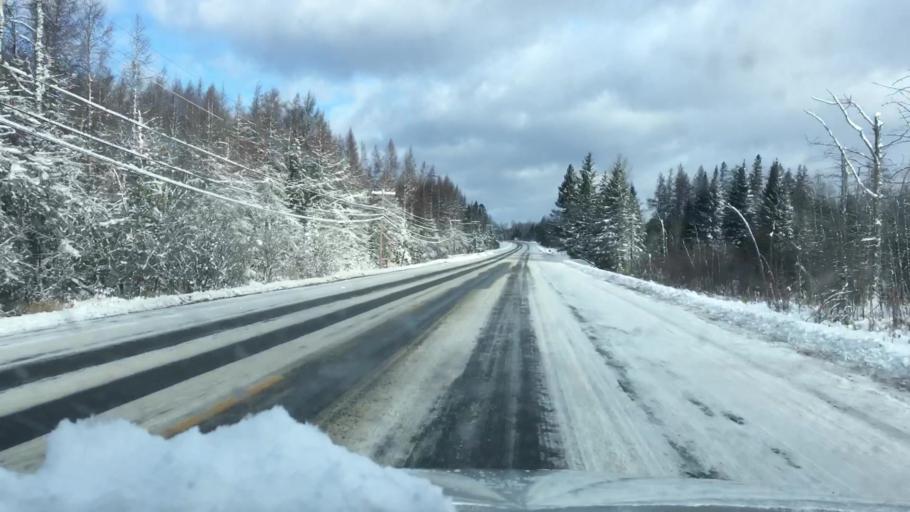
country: US
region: Maine
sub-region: Aroostook County
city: Caribou
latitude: 46.9198
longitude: -68.0192
